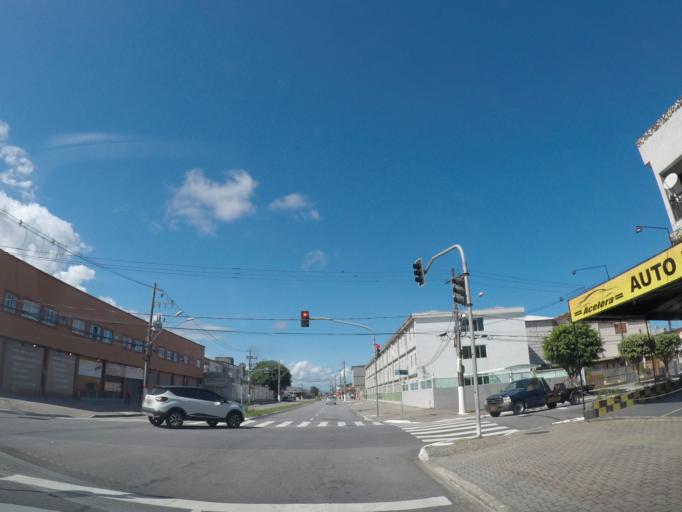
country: BR
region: Sao Paulo
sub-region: Mongagua
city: Mongagua
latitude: -24.0626
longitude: -46.5615
